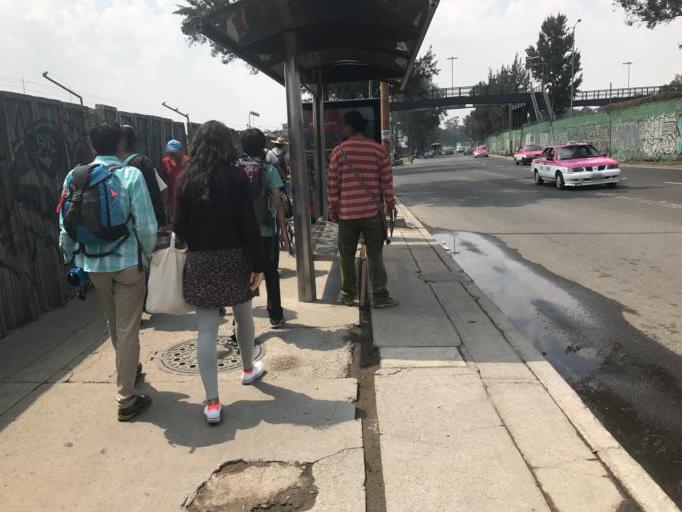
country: MX
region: Mexico City
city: Iztapalapa
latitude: 19.3152
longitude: -99.0775
